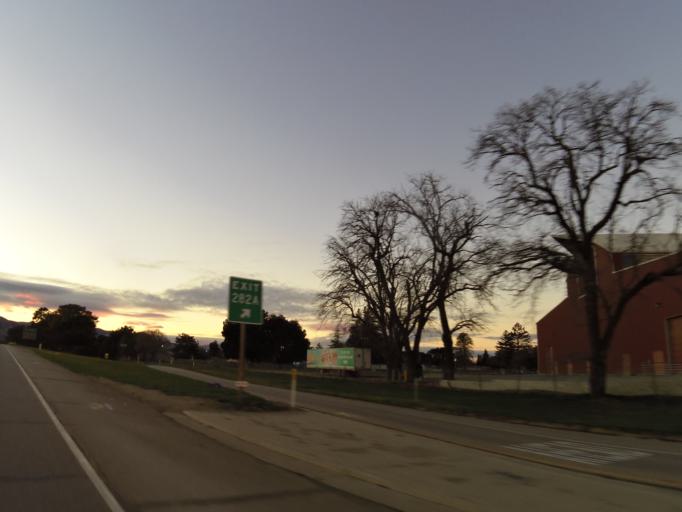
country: US
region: California
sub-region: Monterey County
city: King City
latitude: 36.2031
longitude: -121.1271
